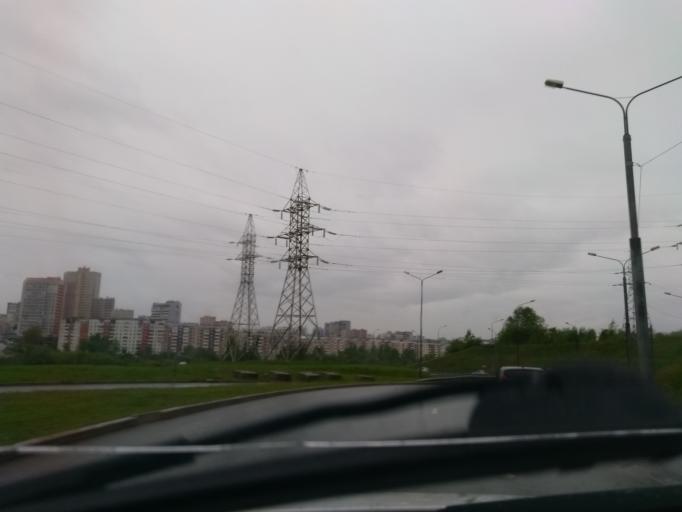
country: RU
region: Perm
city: Perm
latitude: 58.0070
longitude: 56.3212
